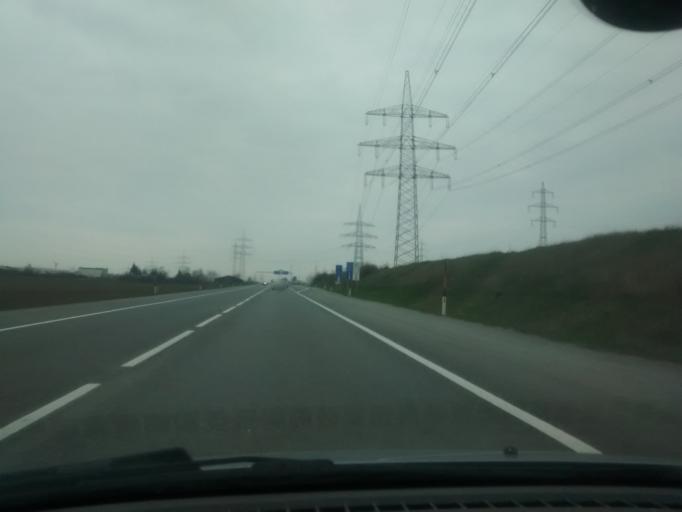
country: AT
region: Lower Austria
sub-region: Politischer Bezirk Wien-Umgebung
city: Leopoldsdorf
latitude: 48.1019
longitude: 16.4122
